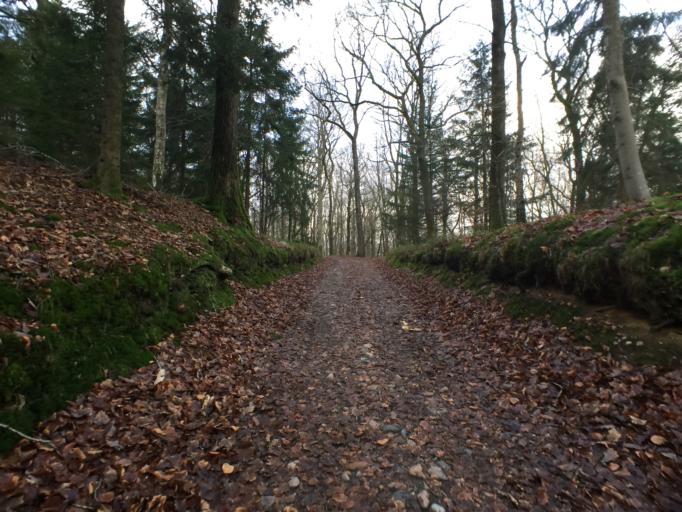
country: DK
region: Central Jutland
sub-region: Silkeborg Kommune
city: Svejbaek
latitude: 56.1081
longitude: 9.6873
